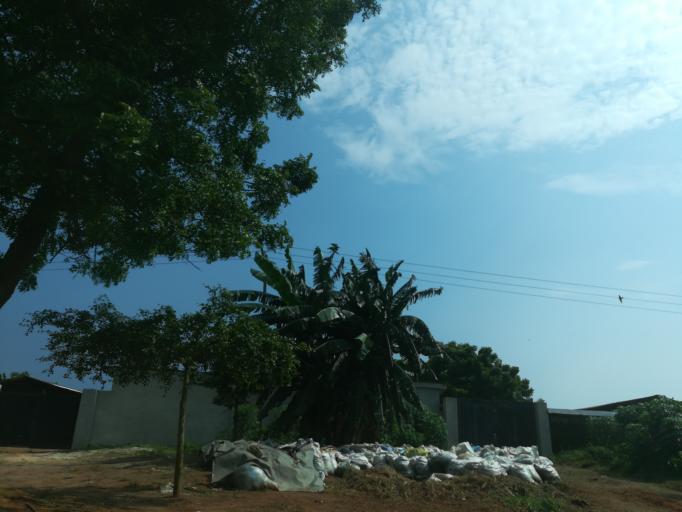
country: NG
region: Lagos
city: Ikorodu
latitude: 6.6078
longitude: 3.6338
